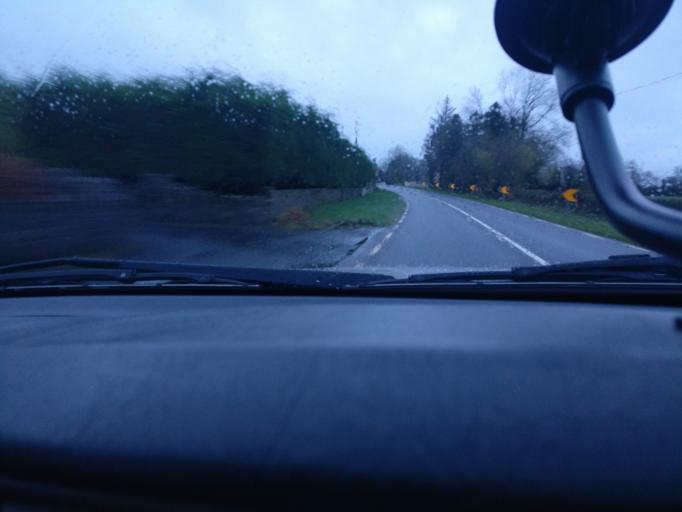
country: IE
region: Connaught
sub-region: County Galway
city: Ballinasloe
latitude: 53.2799
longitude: -8.3720
